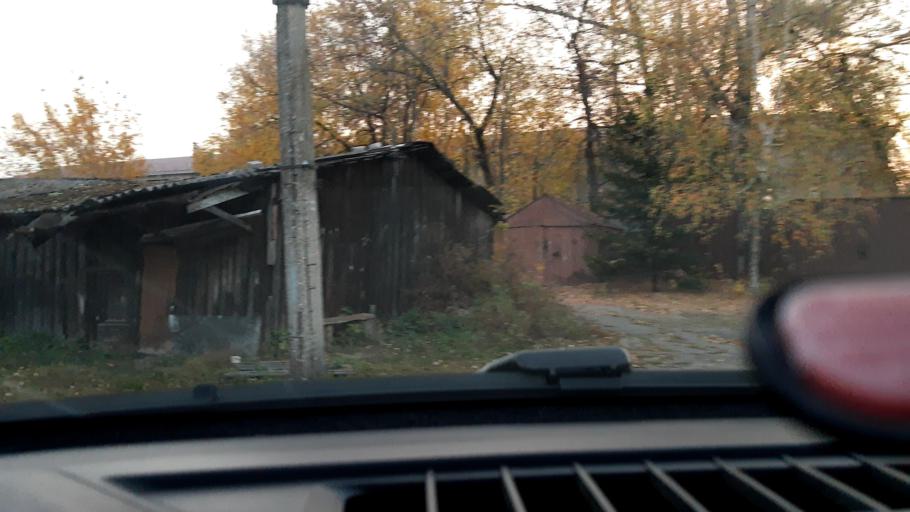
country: RU
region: Nizjnij Novgorod
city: Nizhniy Novgorod
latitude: 56.3047
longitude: 43.8806
